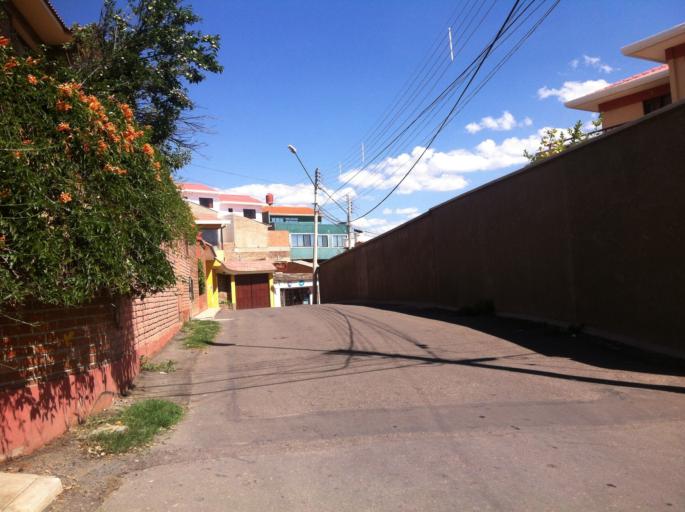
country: BO
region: Cochabamba
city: Cochabamba
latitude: -17.3704
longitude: -66.1353
